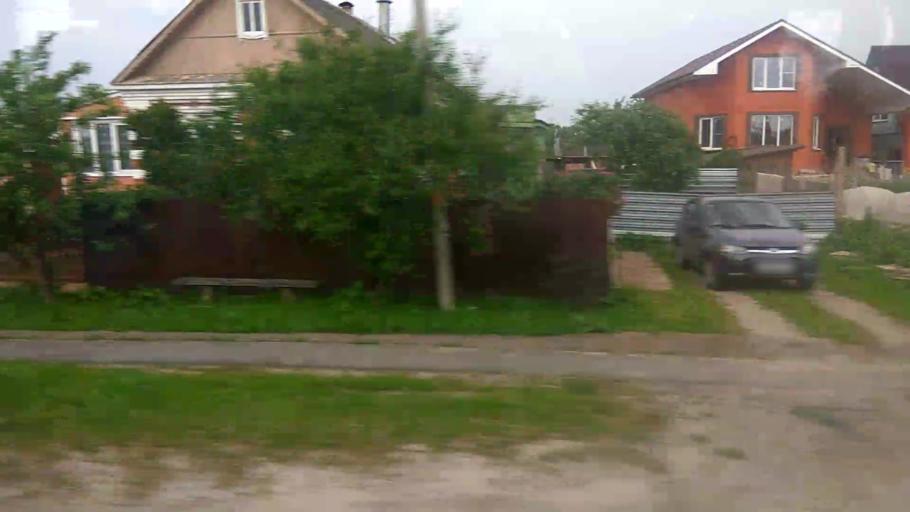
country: RU
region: Moskovskaya
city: Lukhovitsy
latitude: 54.9300
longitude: 39.0031
